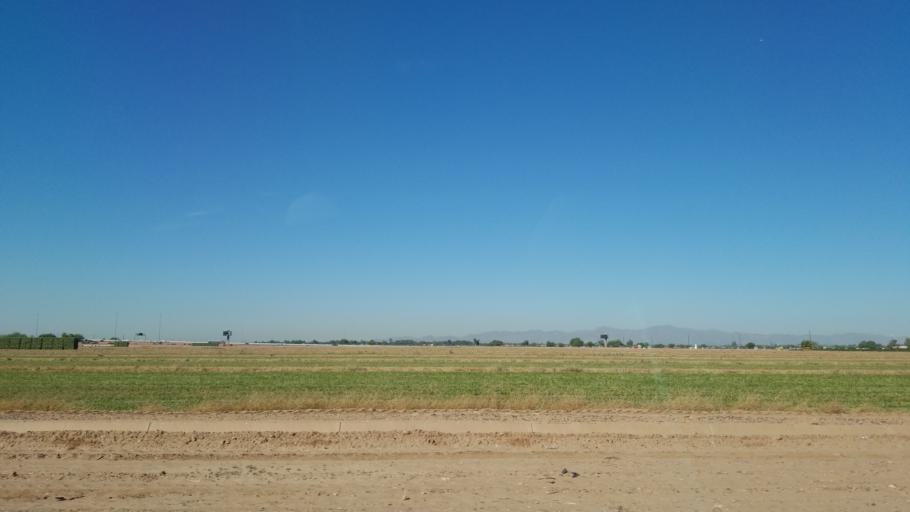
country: US
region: Arizona
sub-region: Maricopa County
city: Tolleson
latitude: 33.4852
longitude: -112.2552
